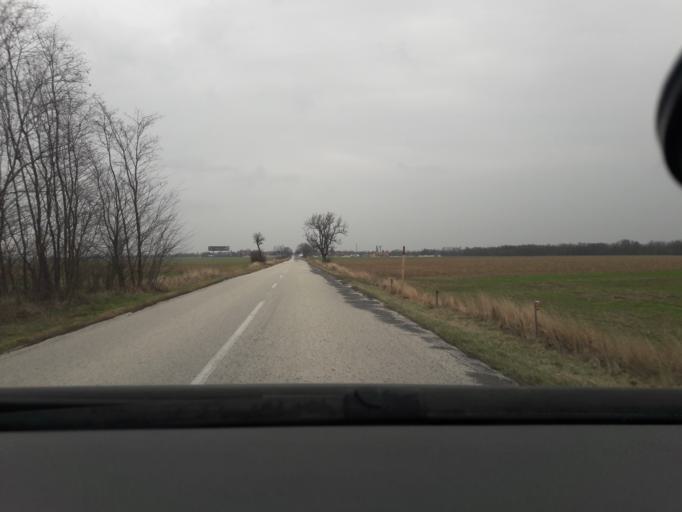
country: SK
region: Bratislavsky
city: Senec
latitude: 48.3241
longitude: 17.4340
